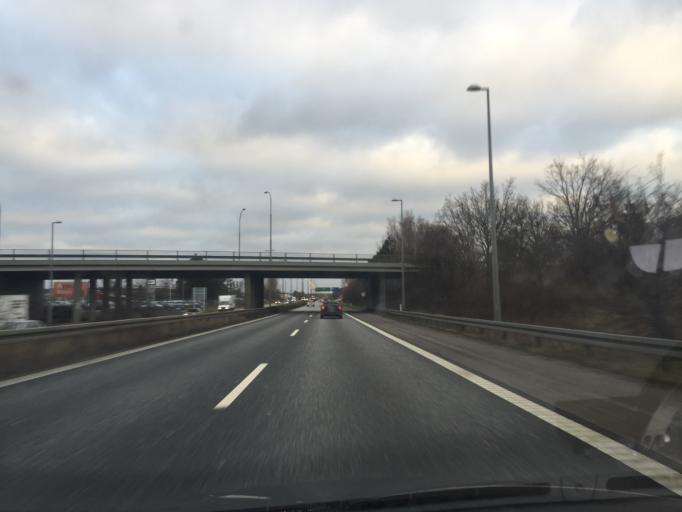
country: DK
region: Capital Region
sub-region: Ishoj Kommune
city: Ishoj
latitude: 55.6163
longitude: 12.3264
